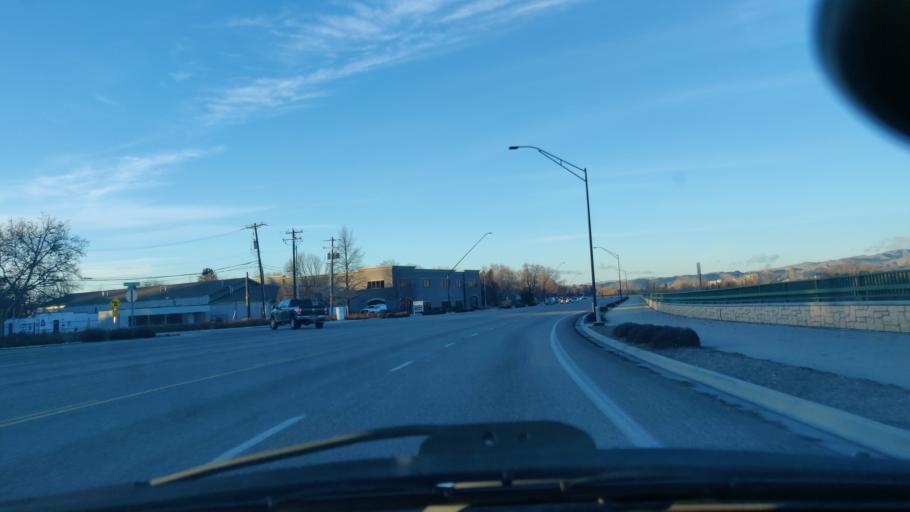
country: US
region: Idaho
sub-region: Ada County
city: Boise
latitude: 43.5787
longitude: -116.1977
